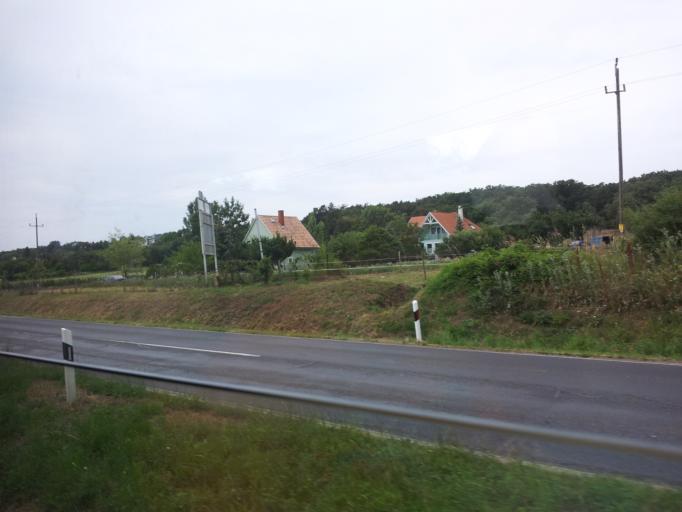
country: HU
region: Veszprem
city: Zanka
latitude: 46.8634
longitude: 17.6747
